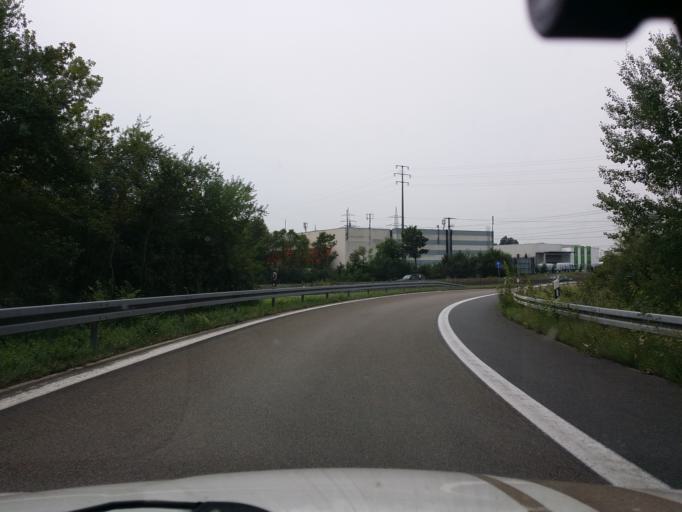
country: DE
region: Baden-Wuerttemberg
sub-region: Karlsruhe Region
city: Weinheim
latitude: 49.5496
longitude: 8.6253
